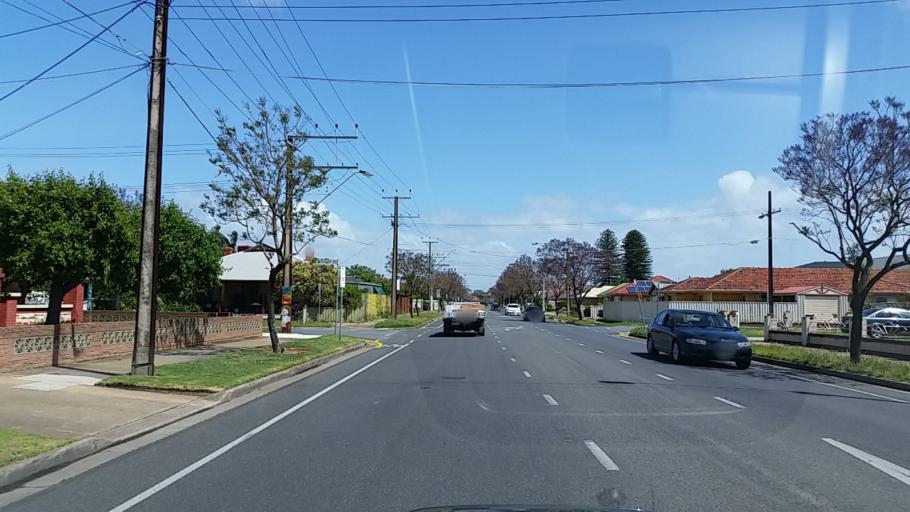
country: AU
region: South Australia
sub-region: Charles Sturt
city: Allenby Gardens
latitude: -34.9005
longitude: 138.5518
